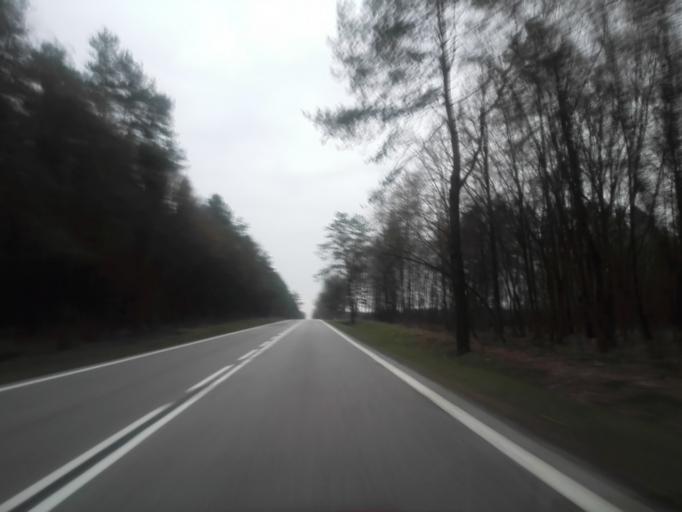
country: PL
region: Podlasie
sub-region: Powiat kolnenski
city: Stawiski
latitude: 53.3343
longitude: 22.1556
